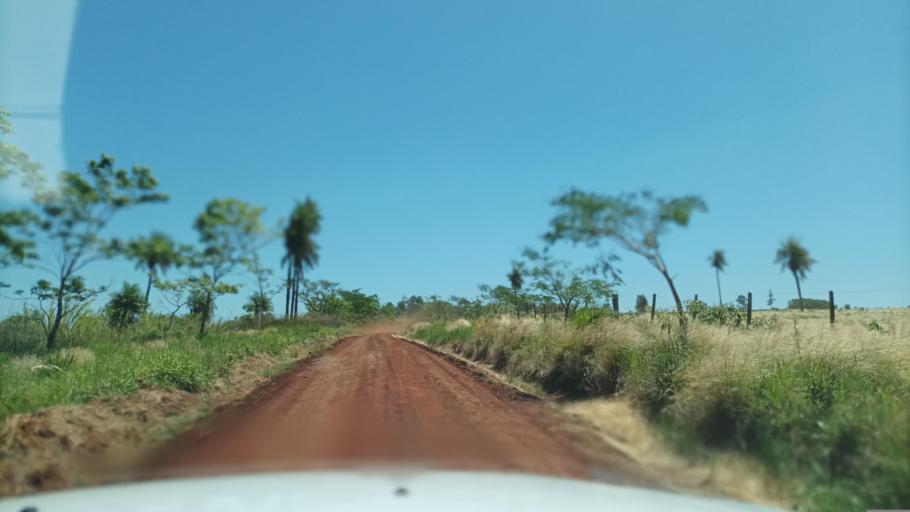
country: AR
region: Misiones
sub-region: Departamento de Apostoles
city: San Jose
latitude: -27.7893
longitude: -55.7100
